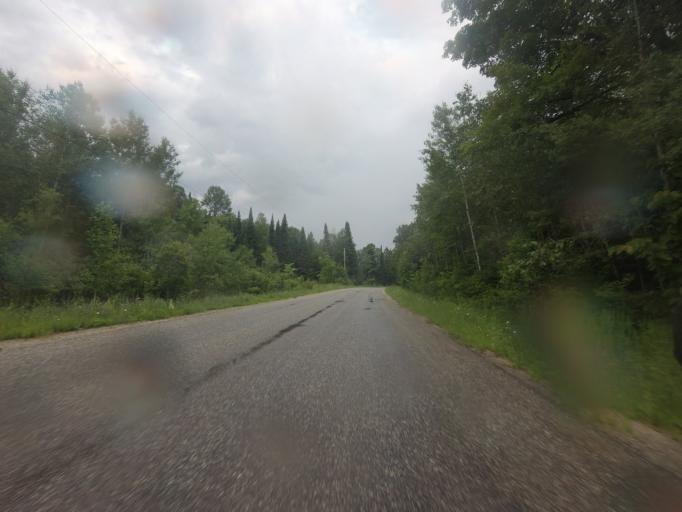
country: CA
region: Quebec
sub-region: Outaouais
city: Maniwaki
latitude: 46.4356
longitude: -75.9426
